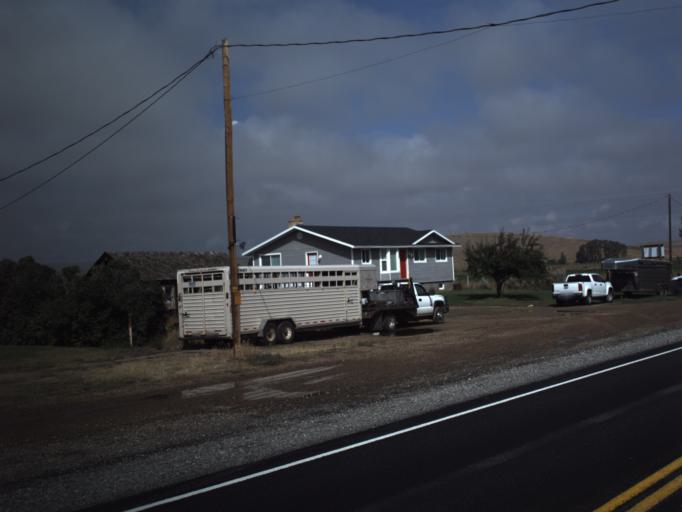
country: US
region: Utah
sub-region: Rich County
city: Randolph
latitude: 41.5255
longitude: -111.1629
